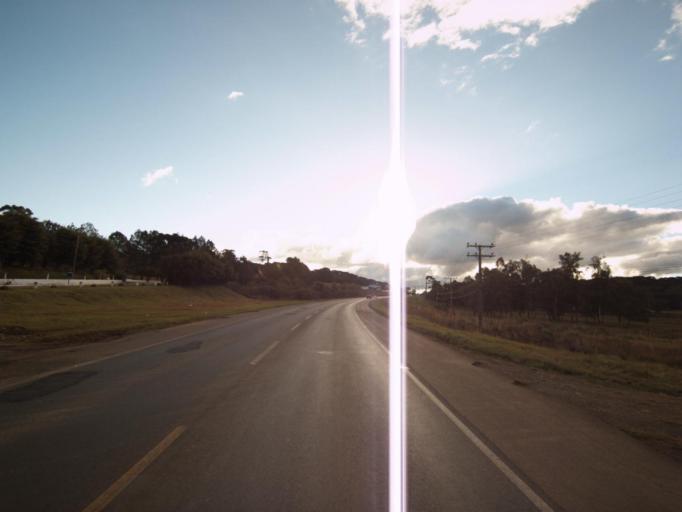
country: BR
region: Santa Catarina
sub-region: Campos Novos
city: Campos Novos
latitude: -27.3920
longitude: -51.1980
